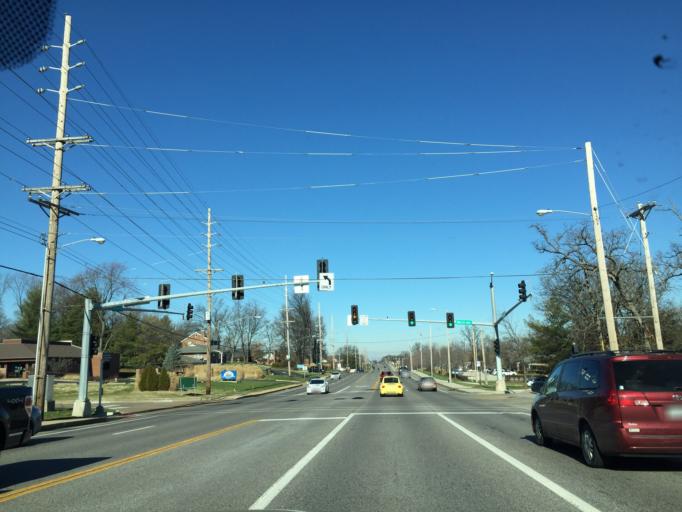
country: US
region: Missouri
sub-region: Saint Louis County
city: Ellisville
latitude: 38.5976
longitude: -90.5857
